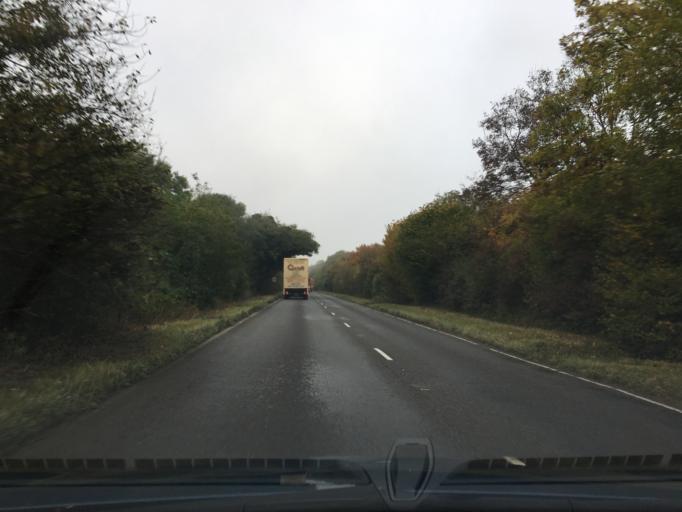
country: GB
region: England
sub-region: Surrey
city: Normandy
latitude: 51.2268
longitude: -0.6475
